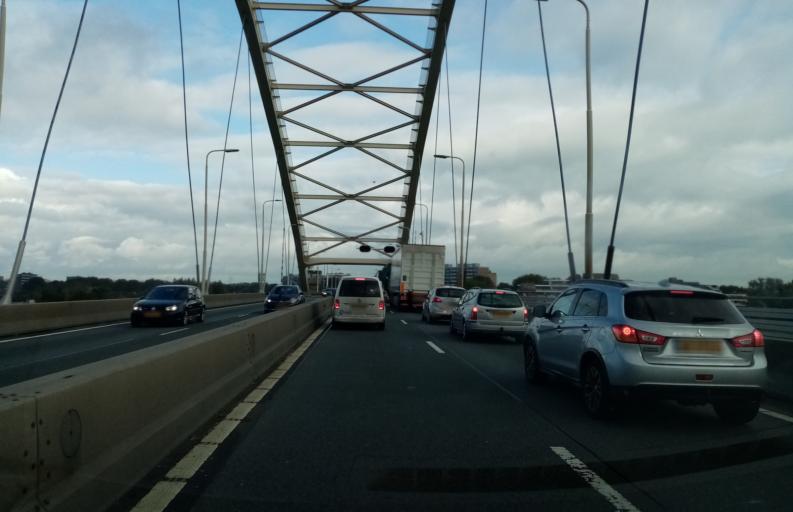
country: NL
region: South Holland
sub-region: Gemeente Papendrecht
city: Papendrecht
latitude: 51.8228
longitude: 4.7059
